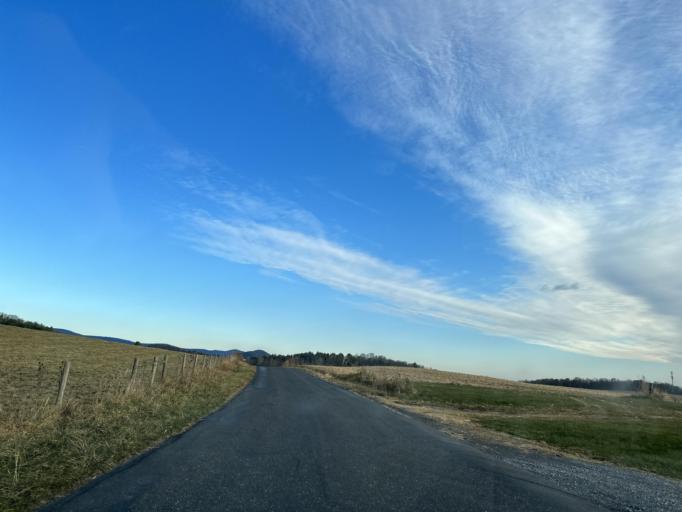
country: US
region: Virginia
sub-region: City of Staunton
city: Staunton
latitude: 38.2331
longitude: -79.2064
